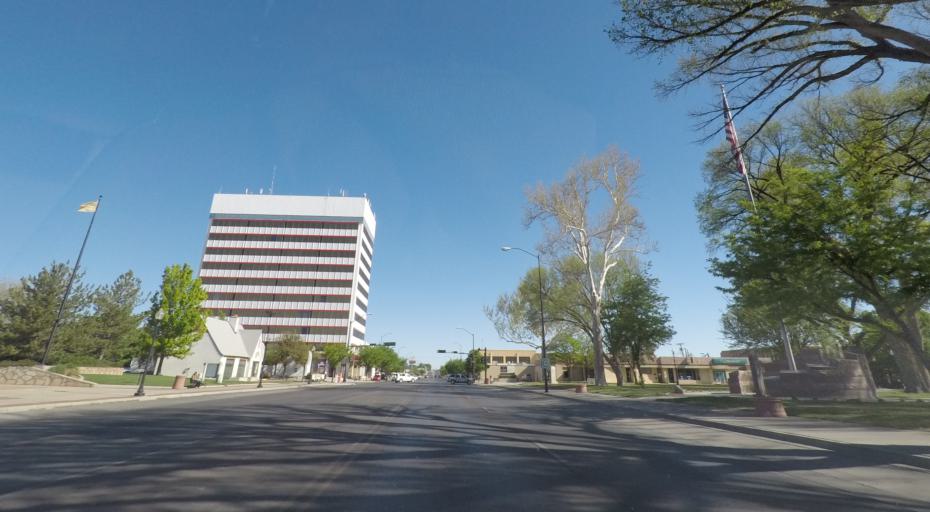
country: US
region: New Mexico
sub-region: Chaves County
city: Roswell
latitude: 33.3968
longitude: -104.5228
